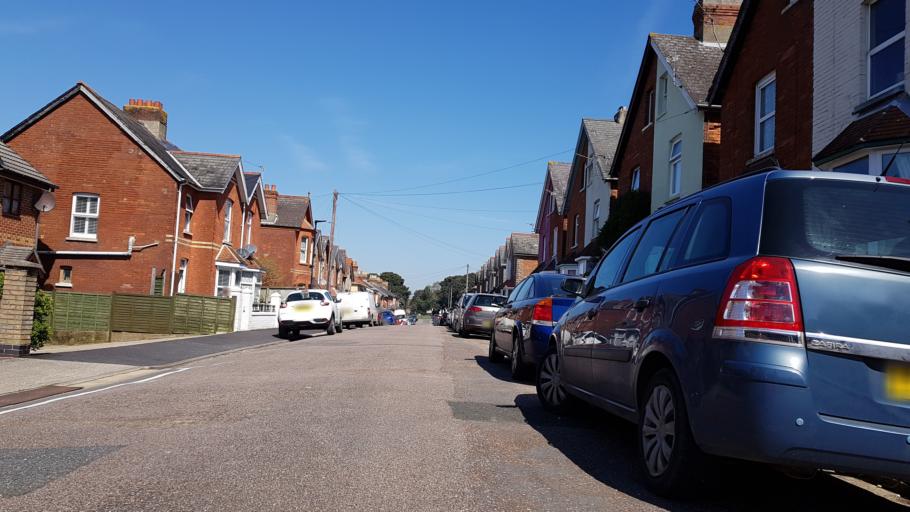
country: GB
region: England
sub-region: Isle of Wight
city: East Cowes
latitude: 50.7528
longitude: -1.2837
